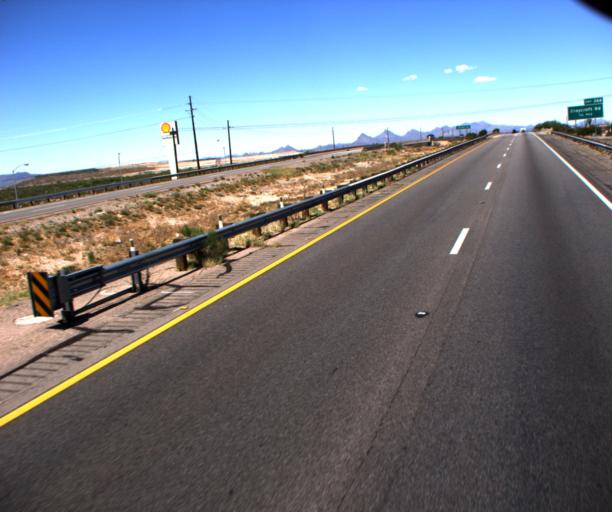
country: US
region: Arizona
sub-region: Pima County
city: Summit
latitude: 32.1138
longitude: -110.8566
